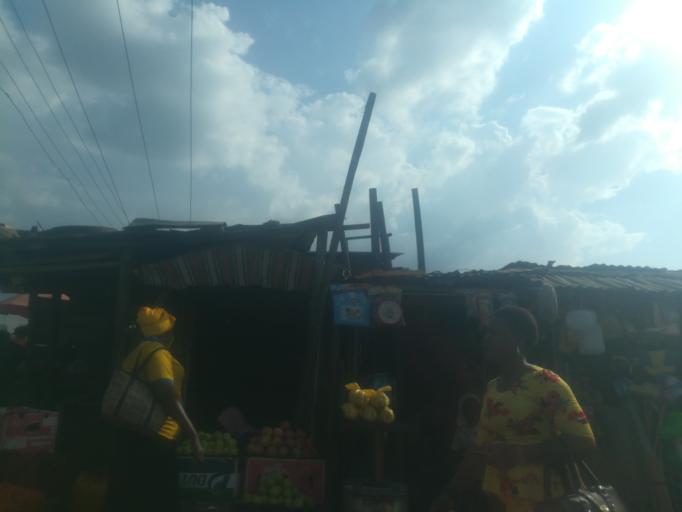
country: NG
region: Oyo
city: Moniya
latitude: 7.5130
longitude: 3.9126
